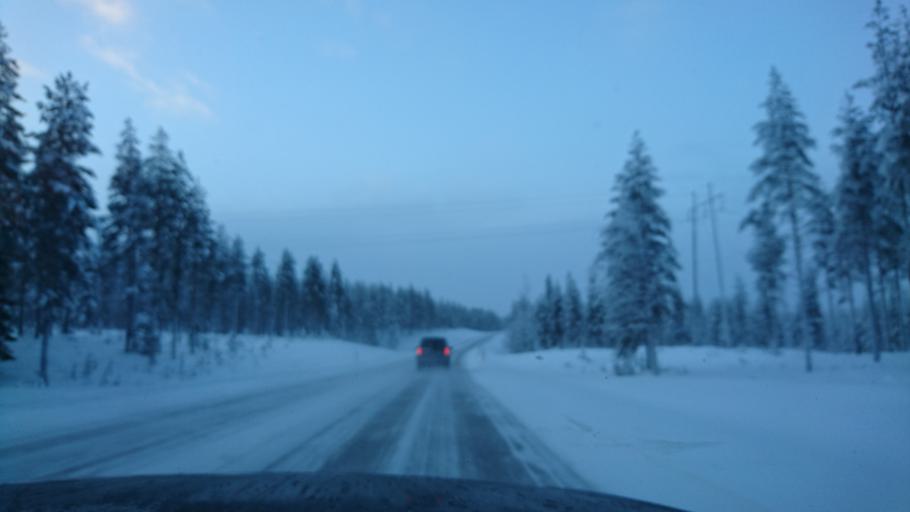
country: FI
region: Northern Ostrobothnia
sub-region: Koillismaa
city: Taivalkoski
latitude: 65.4700
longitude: 27.7291
